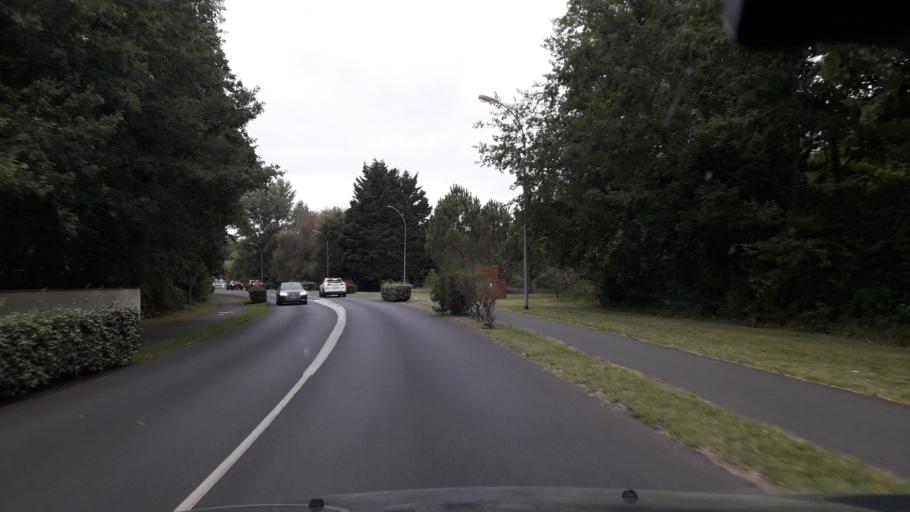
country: FR
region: Poitou-Charentes
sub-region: Departement de la Charente-Maritime
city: Les Mathes
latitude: 45.7151
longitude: -1.1573
